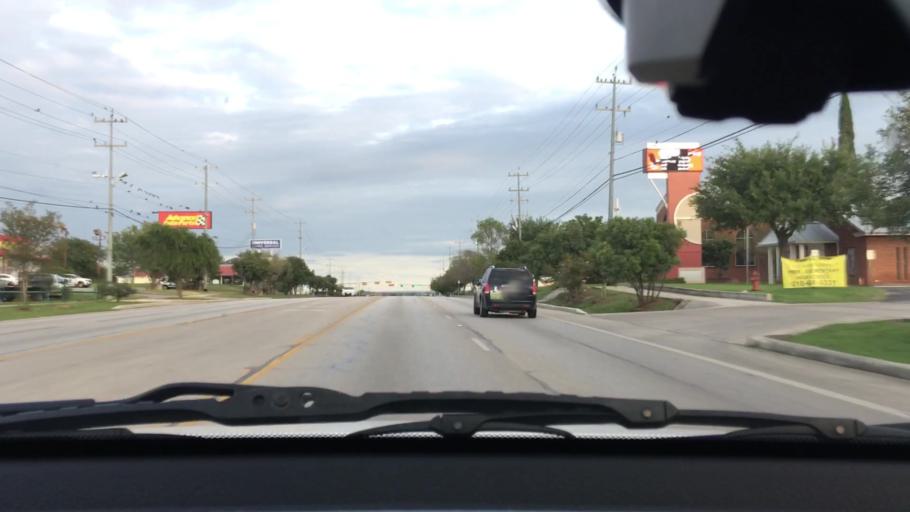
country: US
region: Texas
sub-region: Bexar County
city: Universal City
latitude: 29.5514
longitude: -98.3017
